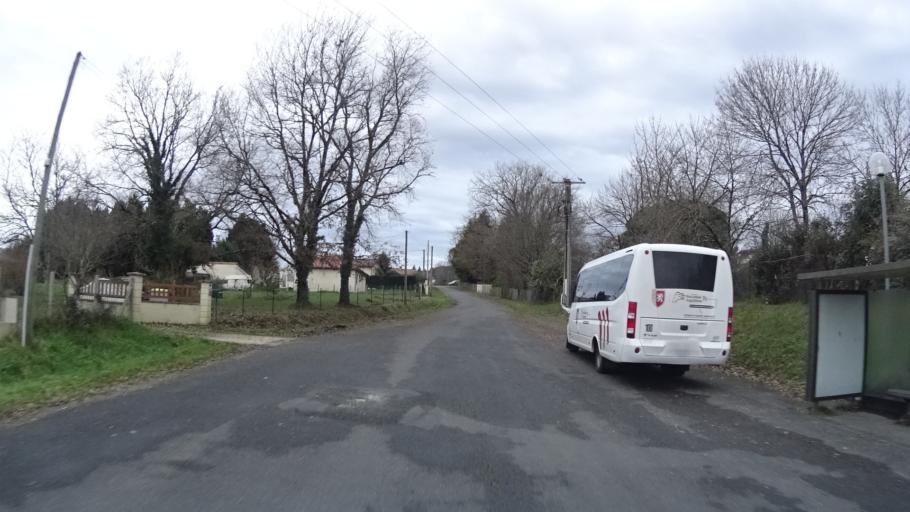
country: FR
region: Aquitaine
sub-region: Departement de la Dordogne
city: Saint-Aulaye
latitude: 45.1992
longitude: 0.1337
